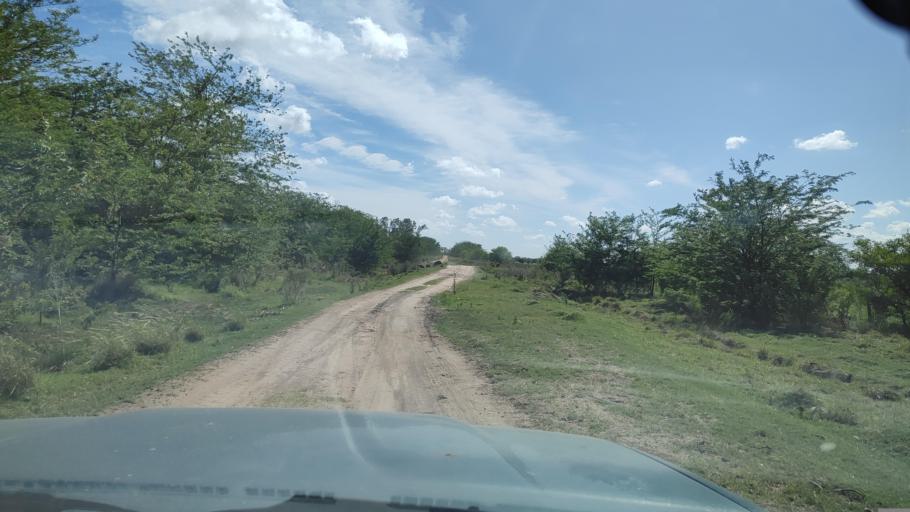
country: AR
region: Buenos Aires
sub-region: Partido de Lujan
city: Lujan
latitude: -34.5217
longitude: -59.1696
